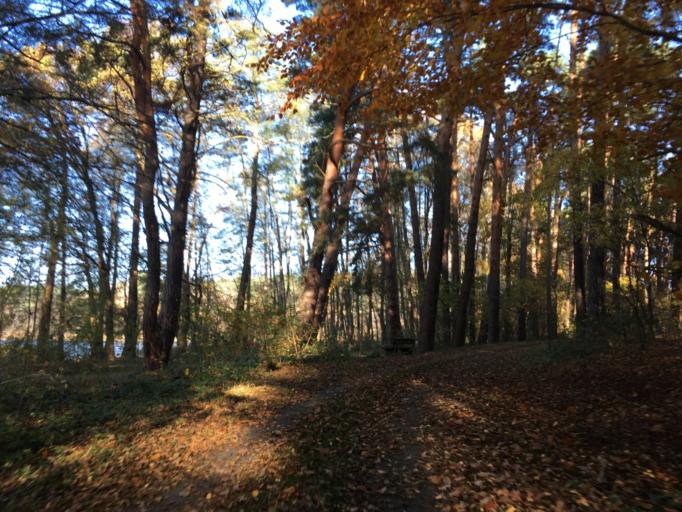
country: DE
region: Brandenburg
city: Wendisch Rietz
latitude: 52.1806
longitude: 14.0009
